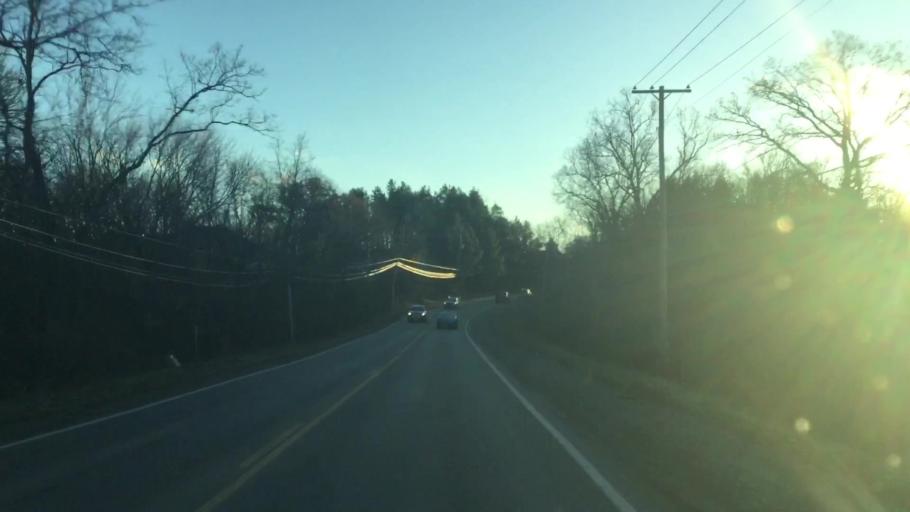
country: US
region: Michigan
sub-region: Genesee County
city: Argentine
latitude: 42.8011
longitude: -83.8224
